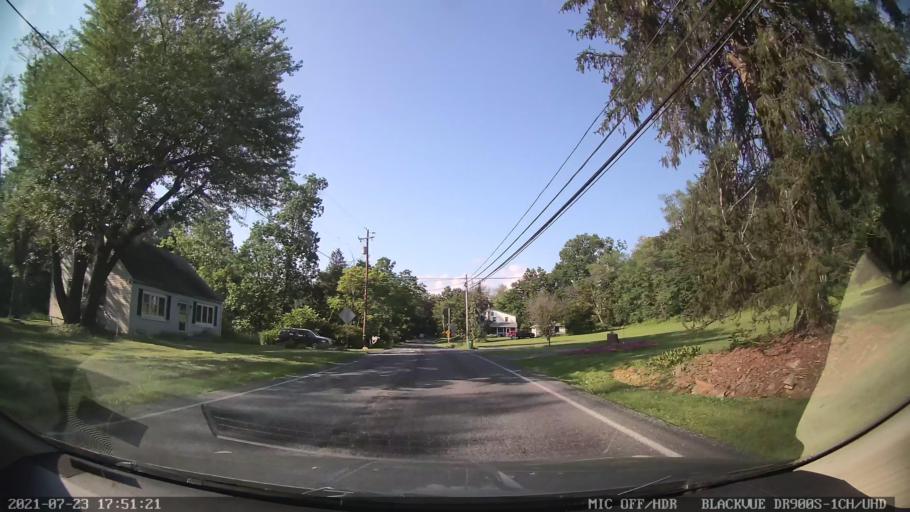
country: US
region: Pennsylvania
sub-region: Lehigh County
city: Alburtis
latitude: 40.4949
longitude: -75.5872
